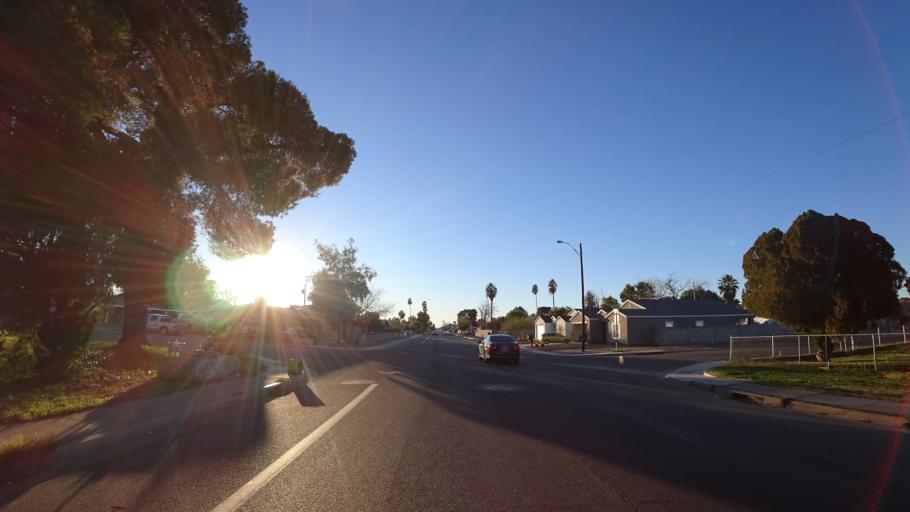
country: US
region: Arizona
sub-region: Maricopa County
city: Phoenix
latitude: 33.4731
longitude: -112.0169
